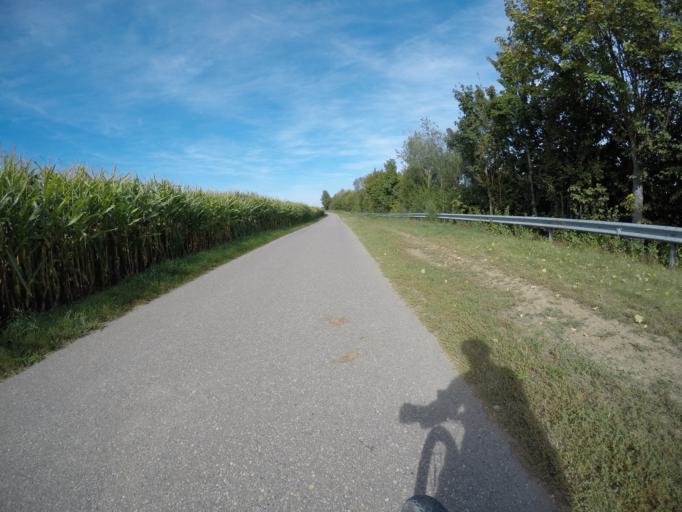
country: DE
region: Baden-Wuerttemberg
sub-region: Regierungsbezirk Stuttgart
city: Moglingen
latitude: 48.8845
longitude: 9.1010
